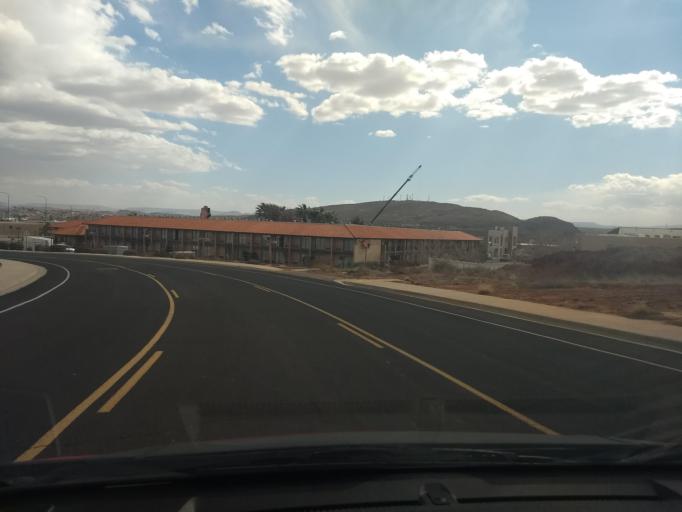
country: US
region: Utah
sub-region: Washington County
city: Saint George
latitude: 37.0852
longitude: -113.5861
